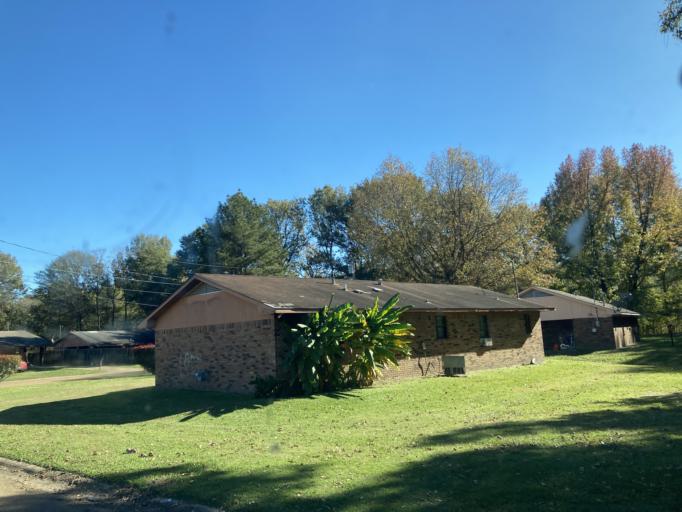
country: US
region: Mississippi
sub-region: Yazoo County
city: Yazoo City
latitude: 32.8409
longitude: -90.4296
